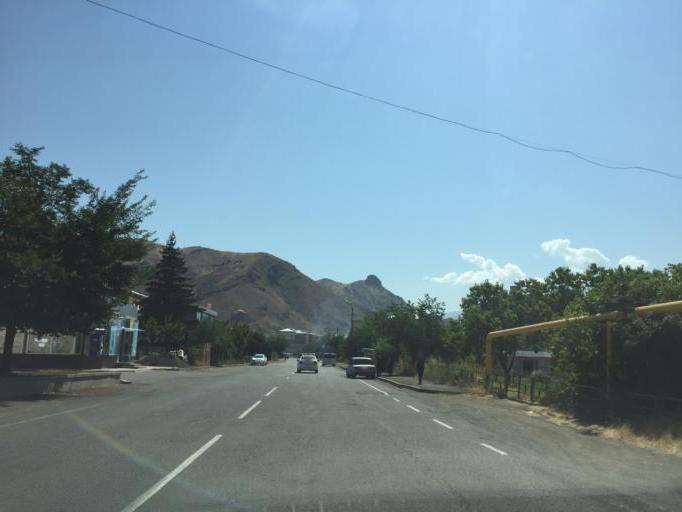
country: AM
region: Vayots' Dzori Marz
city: Vayk'
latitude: 39.6952
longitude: 45.4510
